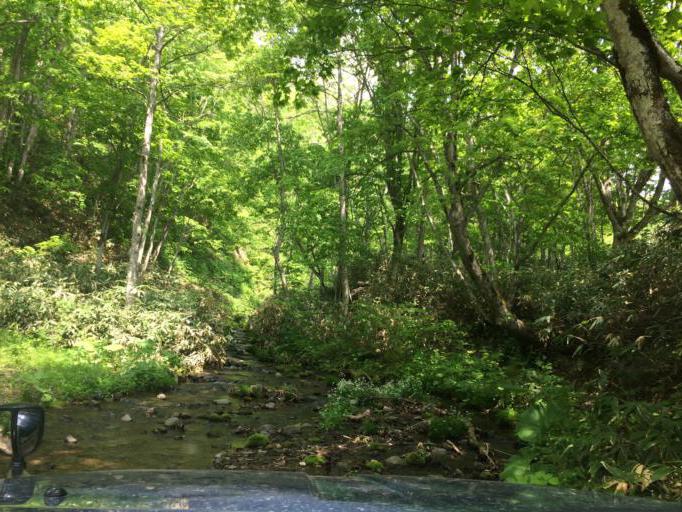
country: JP
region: Hokkaido
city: Niseko Town
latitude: 42.7176
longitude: 140.5572
